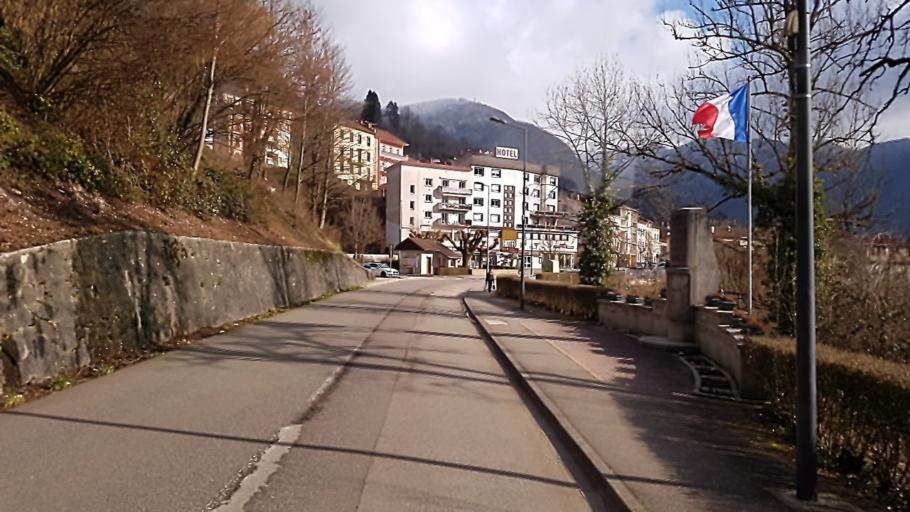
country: FR
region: Franche-Comte
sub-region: Departement du Jura
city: Saint-Claude
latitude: 46.3846
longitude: 5.8694
